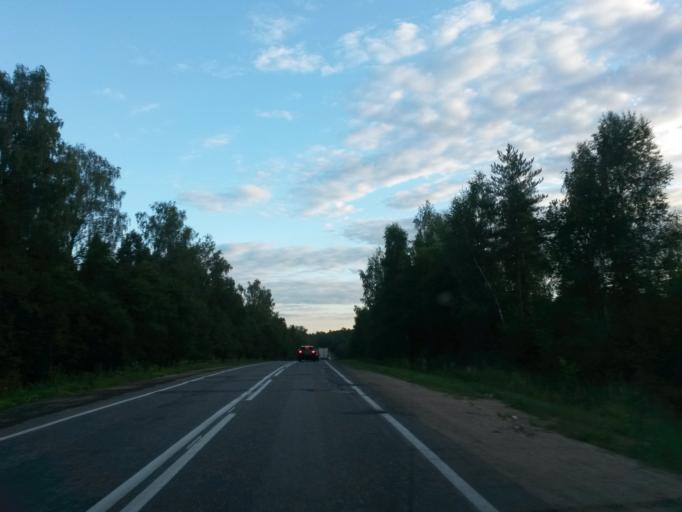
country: RU
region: Jaroslavl
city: Gavrilov-Yam
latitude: 57.3899
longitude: 39.9146
